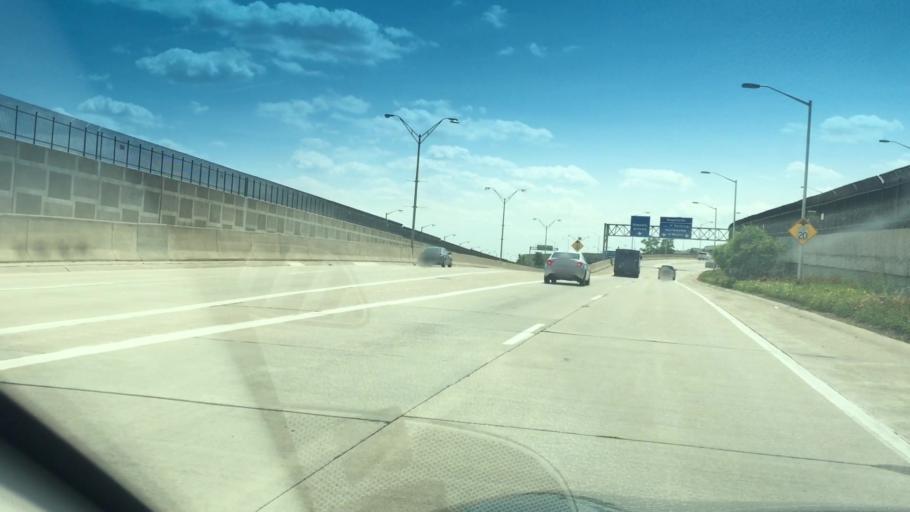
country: US
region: Michigan
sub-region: Wayne County
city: Romulus
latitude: 42.2126
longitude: -83.3508
